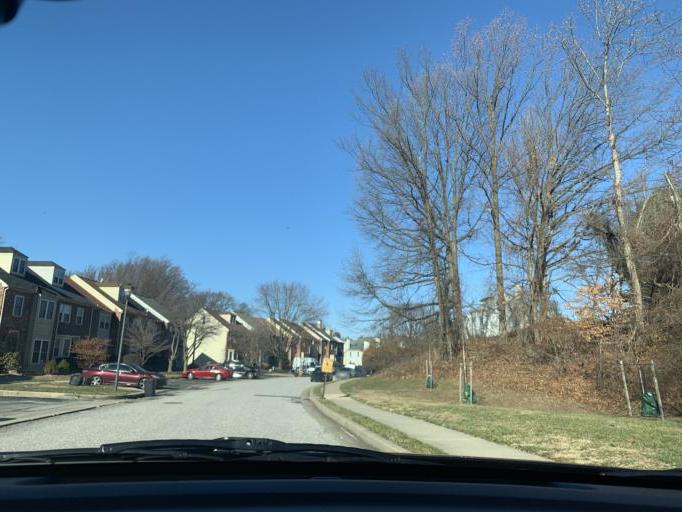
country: US
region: Maryland
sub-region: Baltimore County
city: Garrison
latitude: 39.3956
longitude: -76.7563
